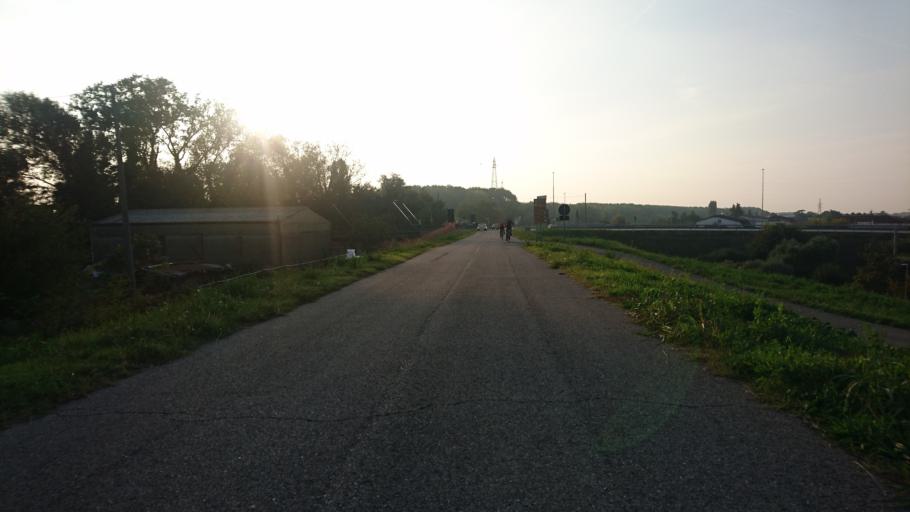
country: IT
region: Veneto
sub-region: Provincia di Rovigo
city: Santa Maria Maddalena
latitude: 44.8903
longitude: 11.6103
